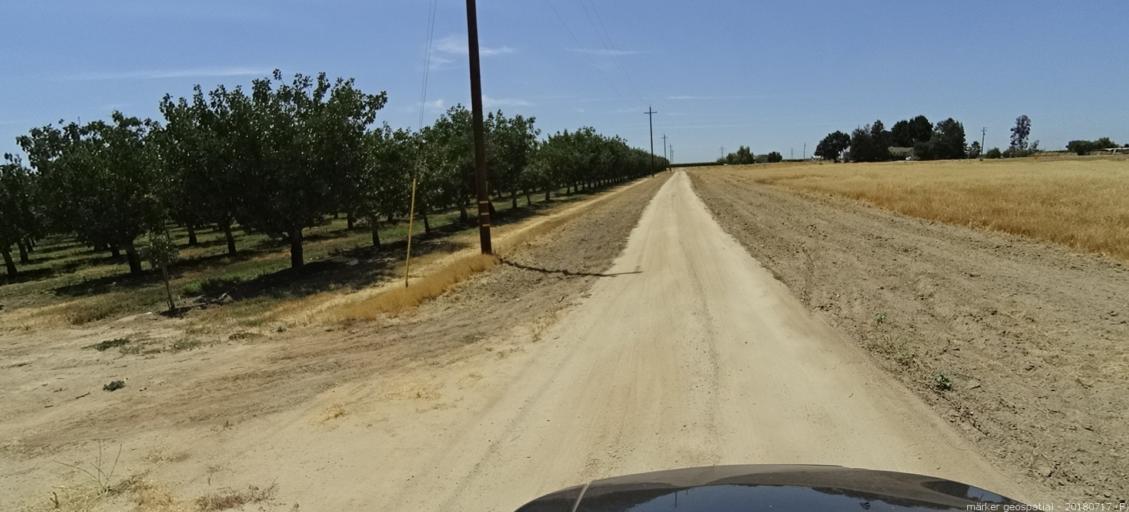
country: US
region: California
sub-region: Madera County
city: Madera Acres
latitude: 37.0527
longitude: -120.1108
